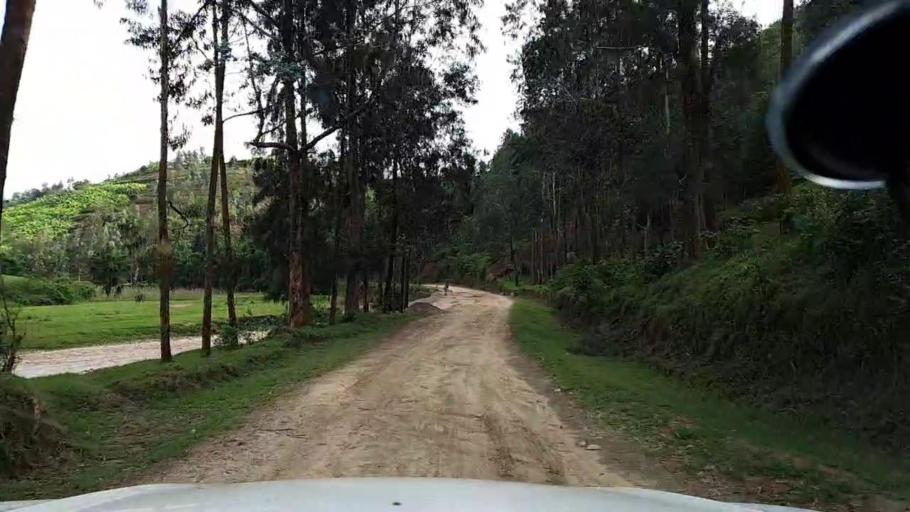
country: RW
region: Western Province
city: Kibuye
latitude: -2.1596
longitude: 29.5460
